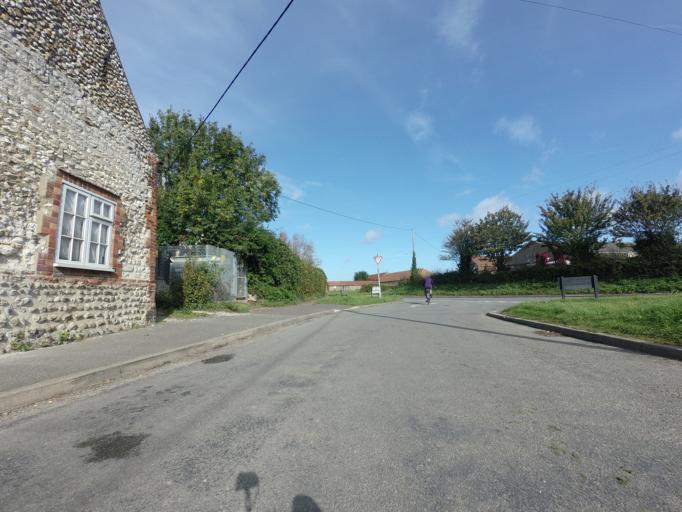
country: GB
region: England
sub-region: Norfolk
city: Wells-next-the-Sea
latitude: 52.9421
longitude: 0.7315
